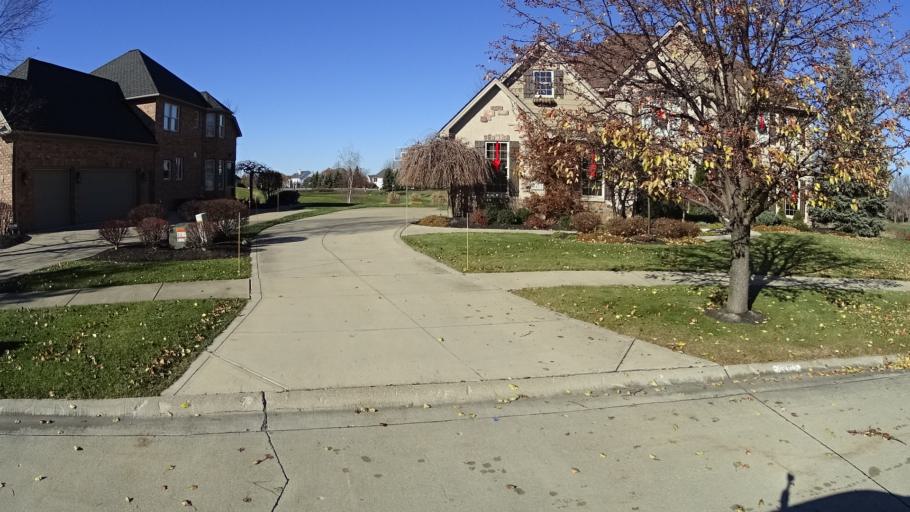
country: US
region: Ohio
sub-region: Lorain County
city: North Ridgeville
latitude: 41.4242
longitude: -81.9957
